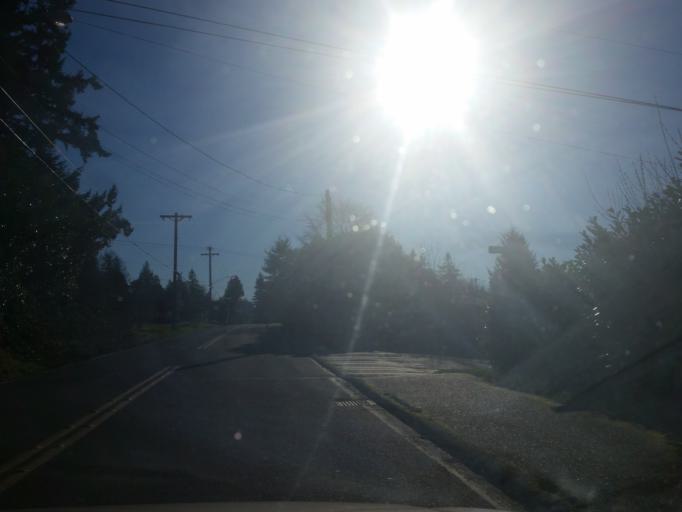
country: US
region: Washington
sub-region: Snohomish County
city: Edmonds
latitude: 47.8270
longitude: -122.3618
